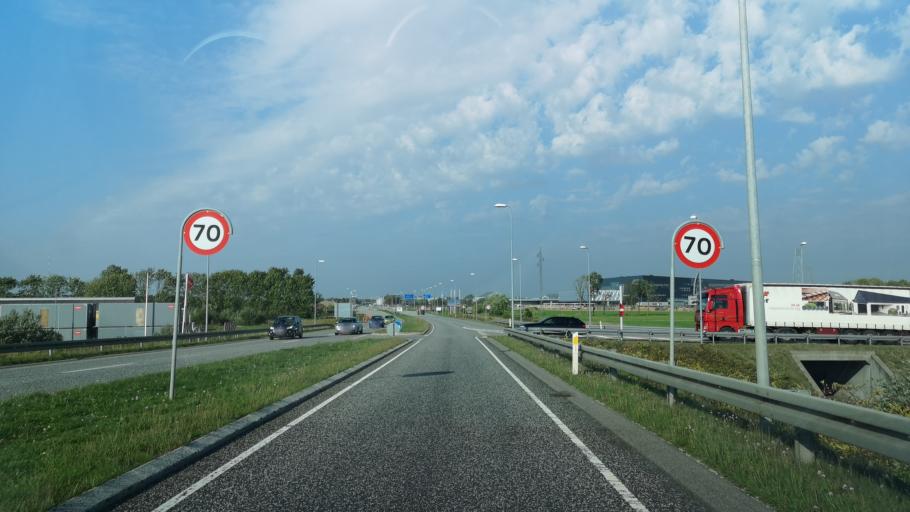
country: DK
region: Central Jutland
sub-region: Herning Kommune
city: Herning
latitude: 56.1136
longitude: 8.9443
